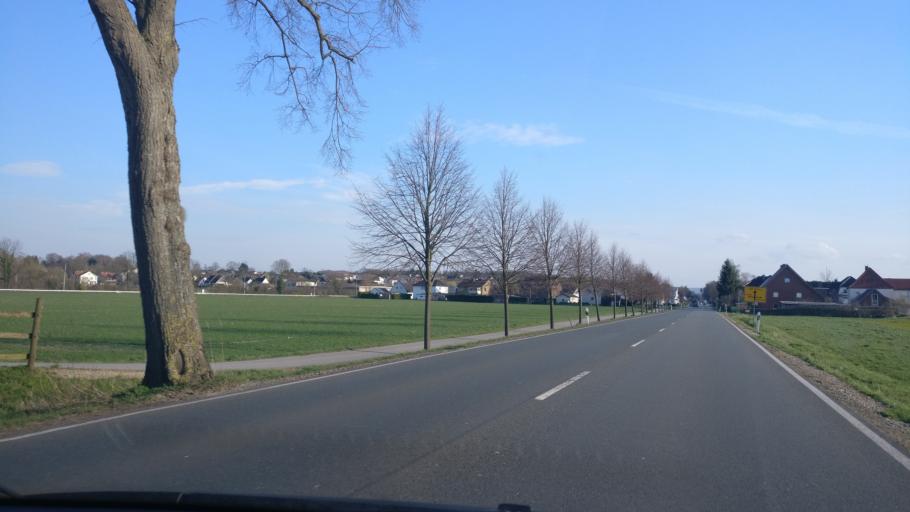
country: DE
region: North Rhine-Westphalia
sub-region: Regierungsbezirk Detmold
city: Lage
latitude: 52.0182
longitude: 8.7650
